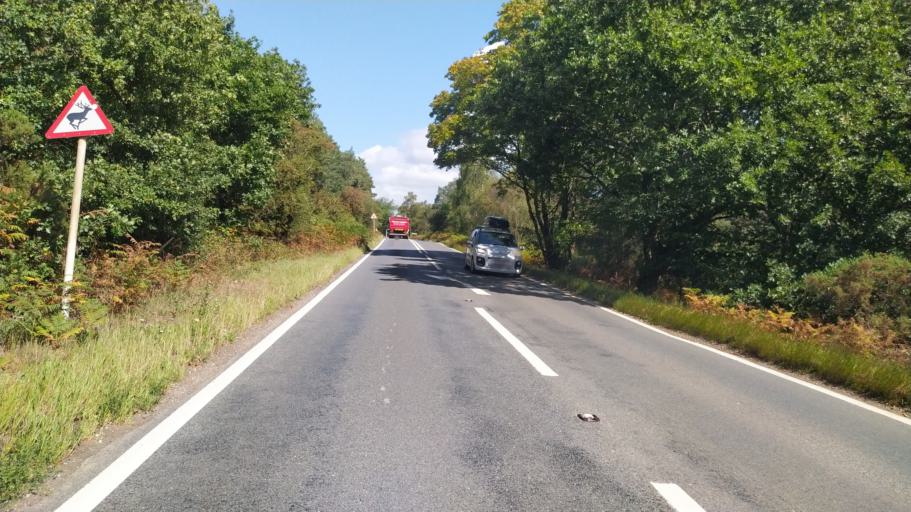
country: GB
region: England
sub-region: Hampshire
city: Bordon
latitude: 51.0818
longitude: -0.8809
